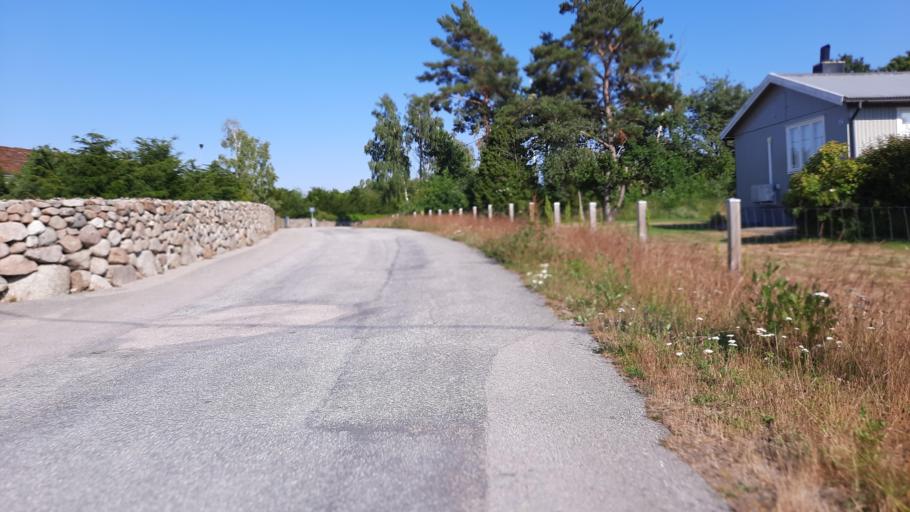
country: SE
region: Blekinge
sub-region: Karlskrona Kommun
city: Sturko
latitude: 56.1243
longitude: 15.6567
